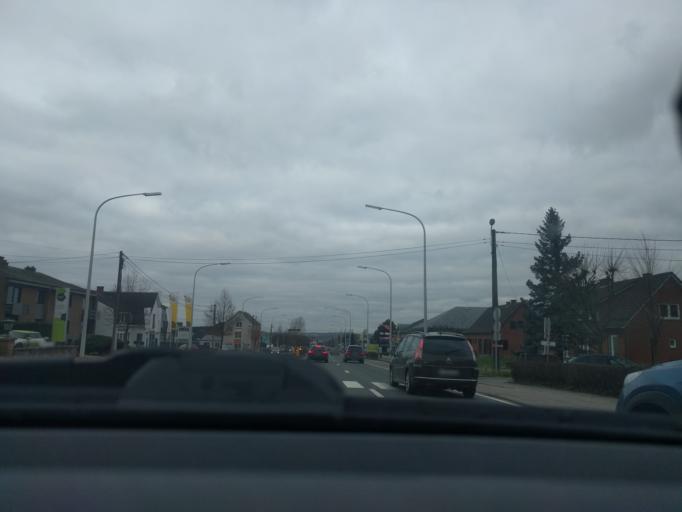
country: BE
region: Wallonia
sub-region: Province de Namur
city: Namur
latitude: 50.4456
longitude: 4.8995
